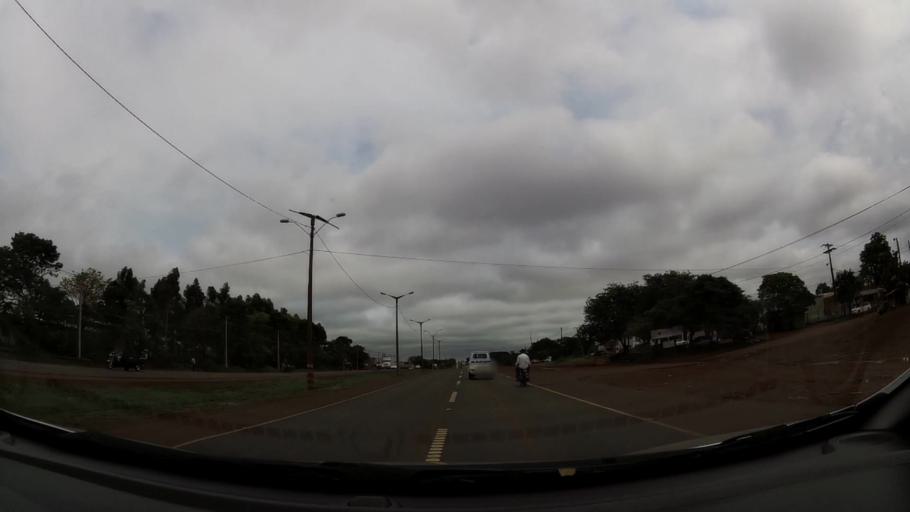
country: PY
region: Alto Parana
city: Ciudad del Este
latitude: -25.4942
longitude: -54.7077
